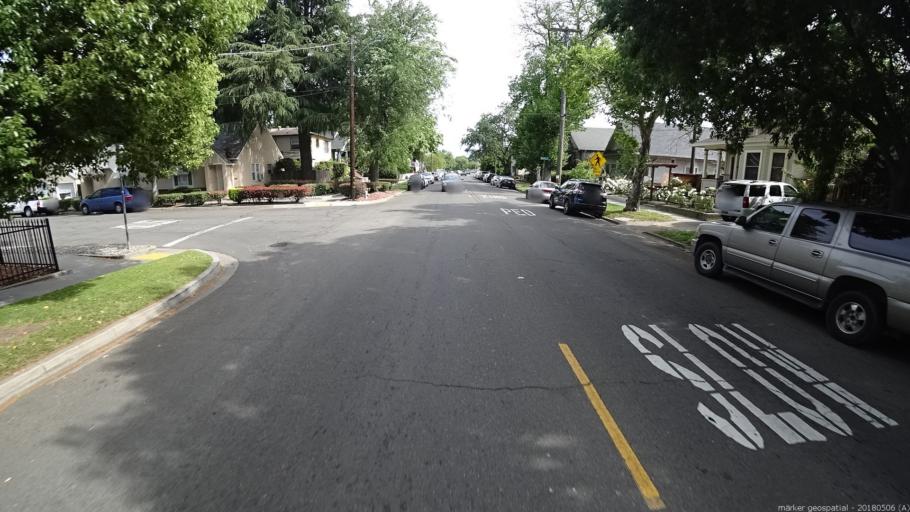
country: US
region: California
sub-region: Sacramento County
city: Sacramento
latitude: 38.5508
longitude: -121.4758
